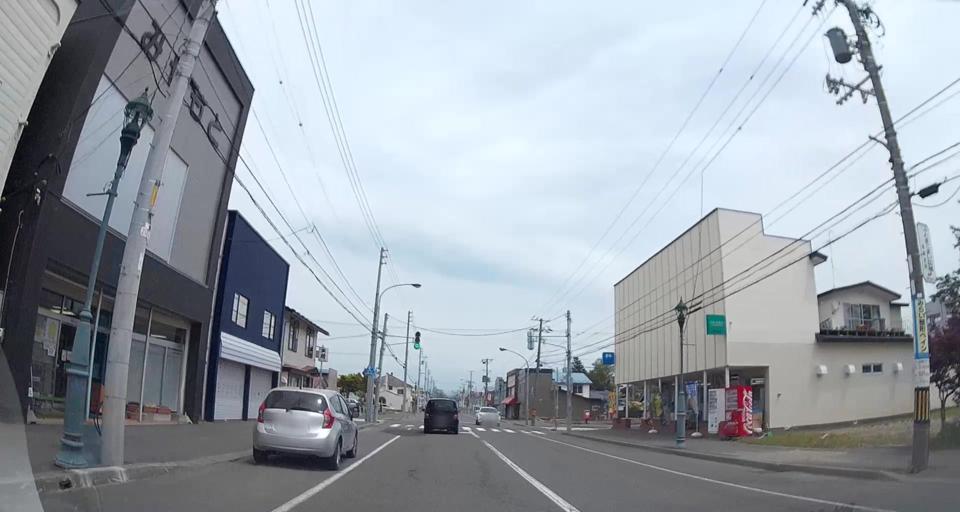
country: JP
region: Hokkaido
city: Chitose
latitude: 42.7648
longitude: 141.8166
